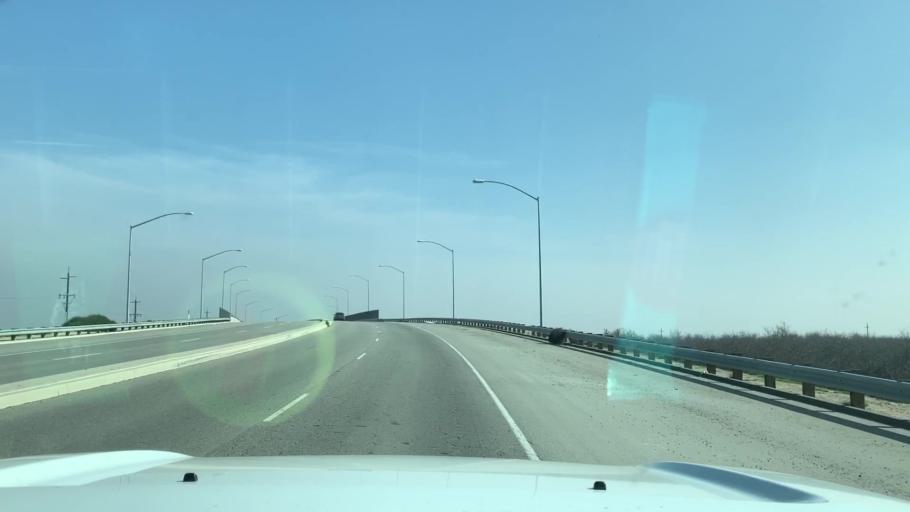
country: US
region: California
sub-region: Kern County
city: Rosedale
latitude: 35.4411
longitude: -119.2012
